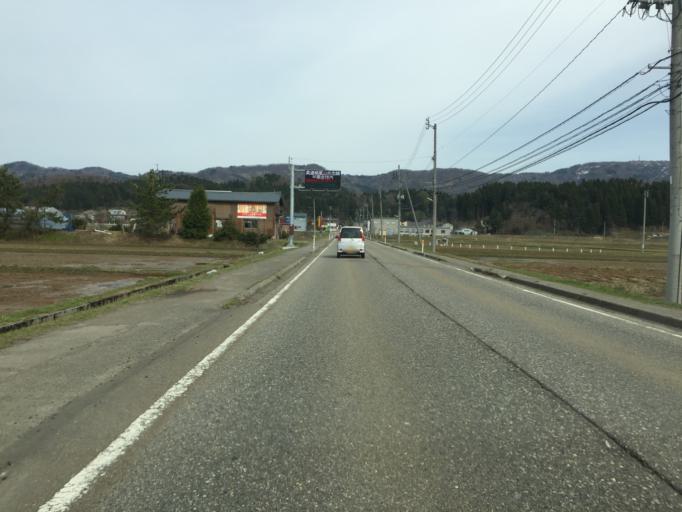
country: JP
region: Niigata
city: Nagaoka
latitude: 37.4541
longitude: 138.8920
